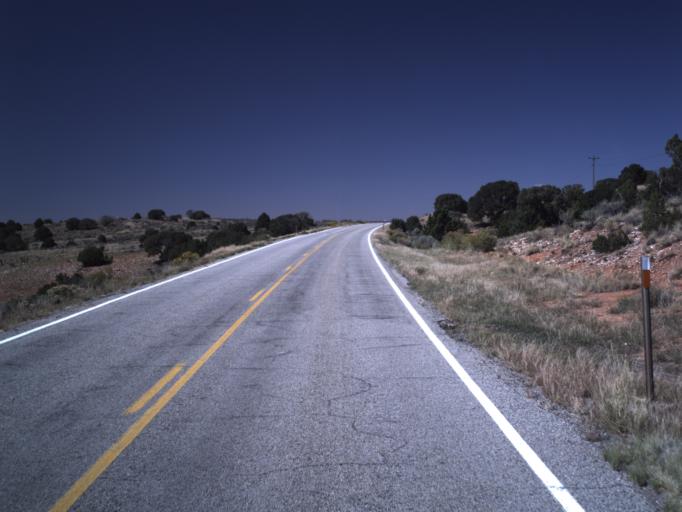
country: US
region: Utah
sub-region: Grand County
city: Moab
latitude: 38.3058
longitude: -109.3935
